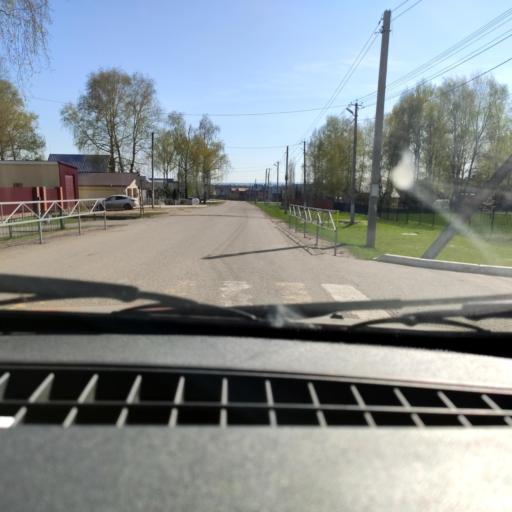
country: RU
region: Bashkortostan
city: Kabakovo
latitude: 54.5949
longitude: 56.1790
